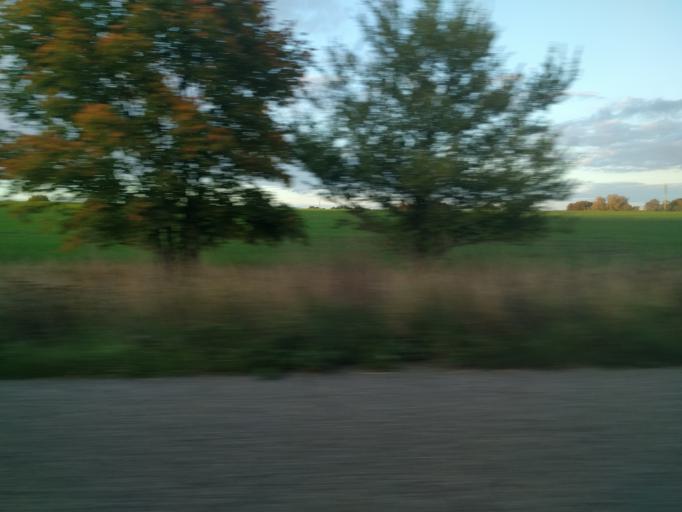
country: DK
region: South Denmark
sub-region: Nyborg Kommune
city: Ullerslev
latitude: 55.3453
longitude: 10.6432
